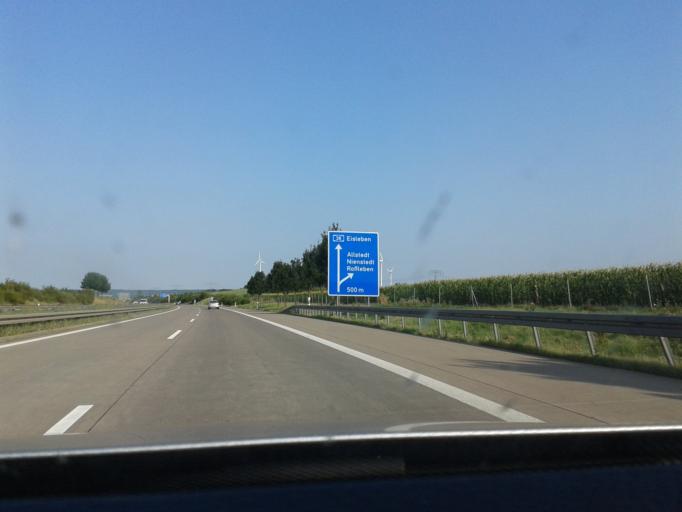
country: DE
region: Saxony-Anhalt
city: Allstedt
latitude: 51.4306
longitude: 11.3790
